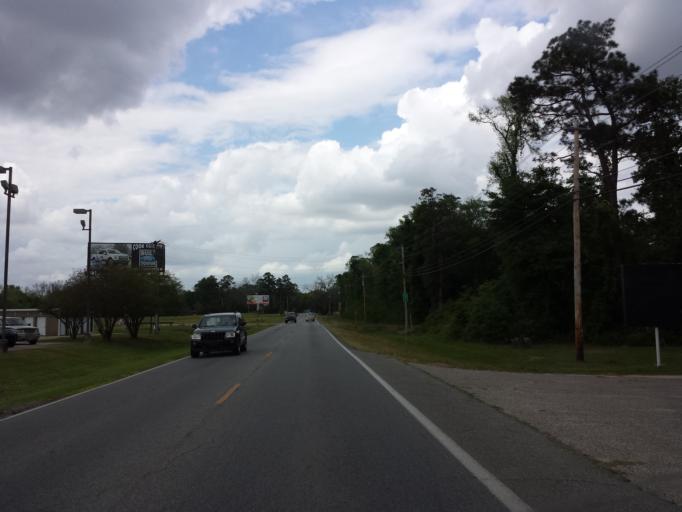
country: US
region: Georgia
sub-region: Cook County
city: Adel
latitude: 31.1260
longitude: -83.4195
